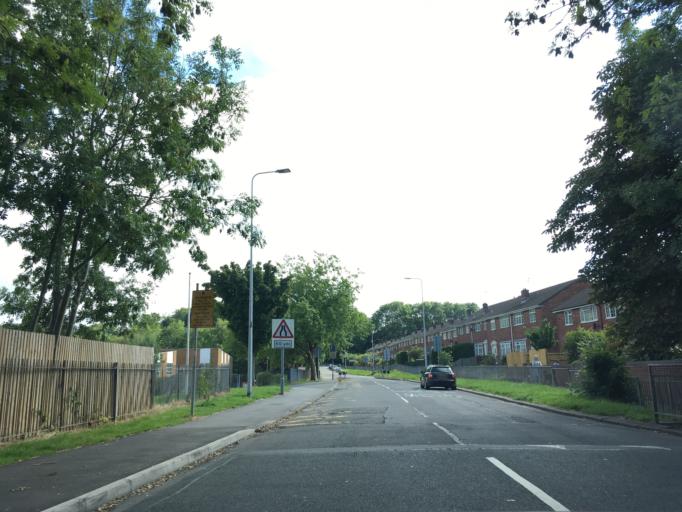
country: GB
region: Wales
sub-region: Cardiff
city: Cardiff
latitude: 51.5154
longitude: -3.1582
